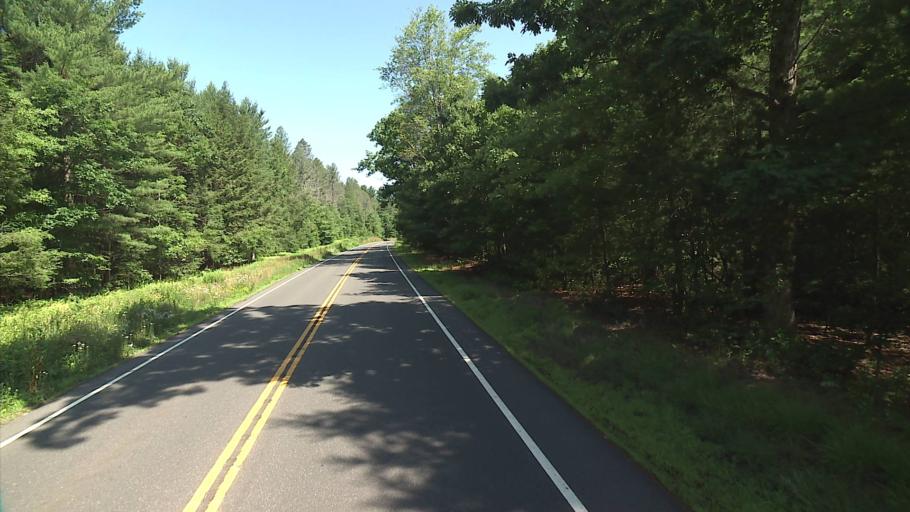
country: US
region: Connecticut
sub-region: Litchfield County
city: Terryville
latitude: 41.7089
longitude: -73.0109
